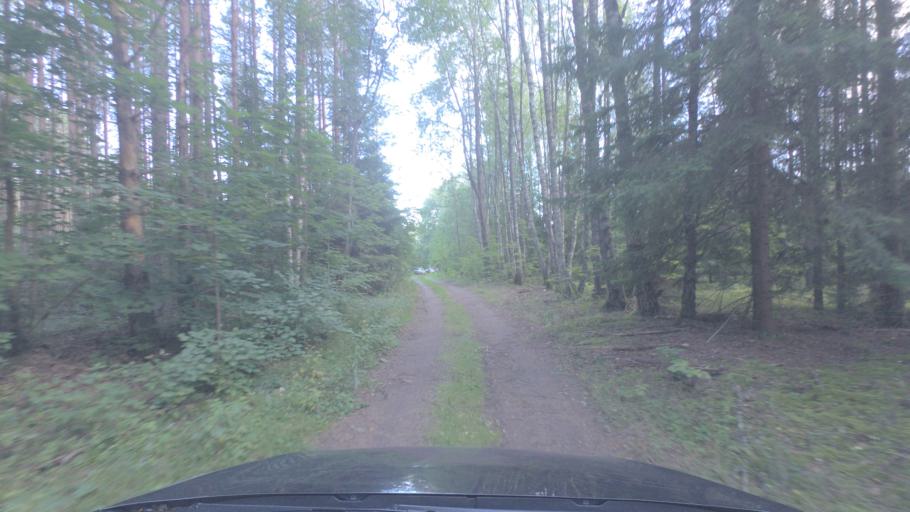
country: LT
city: Svencioneliai
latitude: 55.1602
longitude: 25.8529
